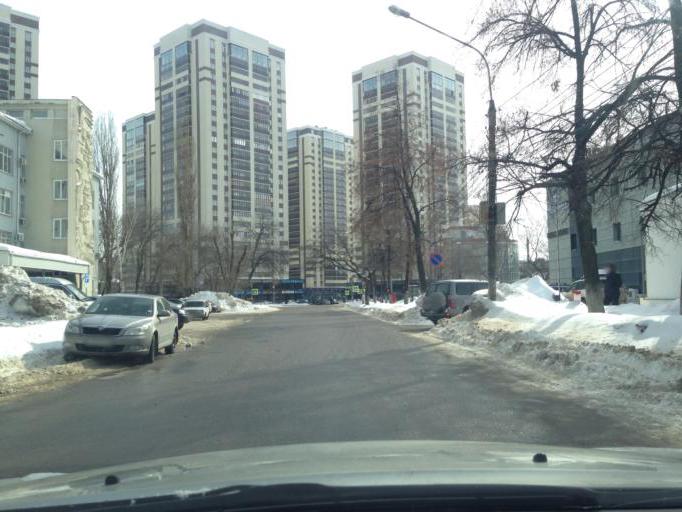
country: RU
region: Voronezj
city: Voronezh
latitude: 51.6563
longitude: 39.1774
